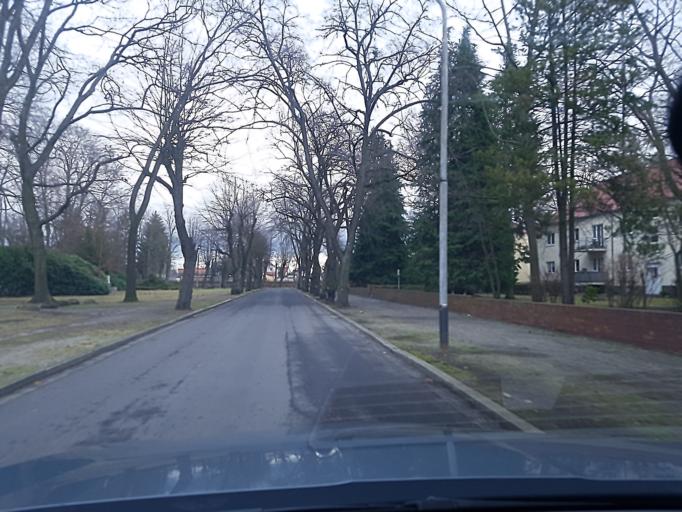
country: DE
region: Brandenburg
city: Finsterwalde
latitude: 51.6320
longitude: 13.6946
